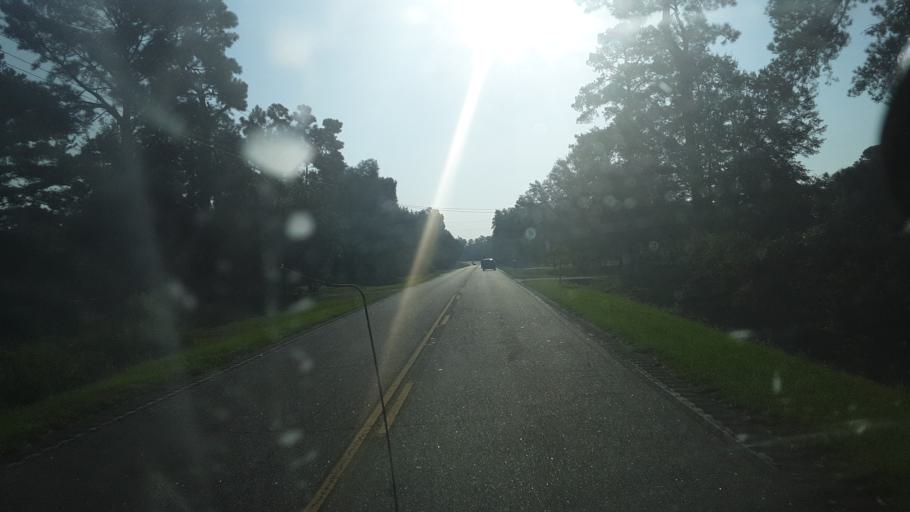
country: US
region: South Carolina
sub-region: Horry County
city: Red Hill
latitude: 33.8219
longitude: -78.9098
